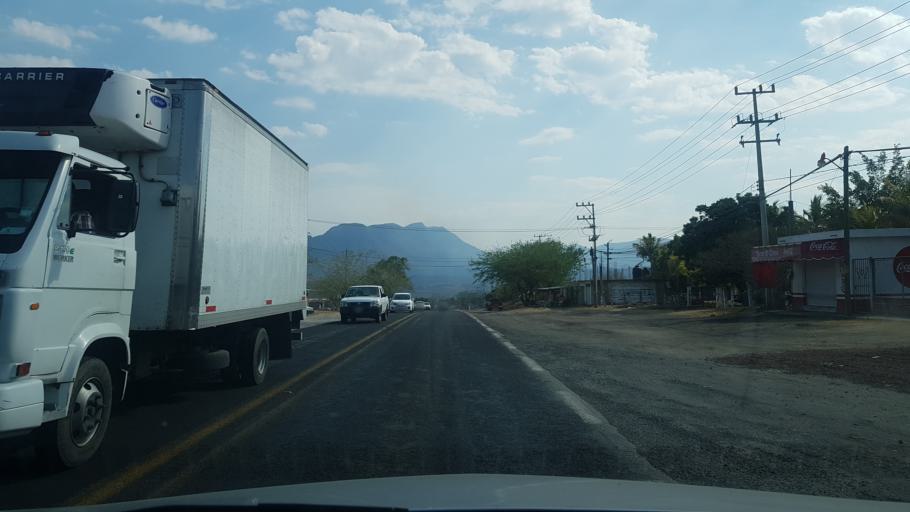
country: MX
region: Morelos
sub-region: Amacuzac
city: Amacuzac
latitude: 18.6081
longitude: -99.3625
